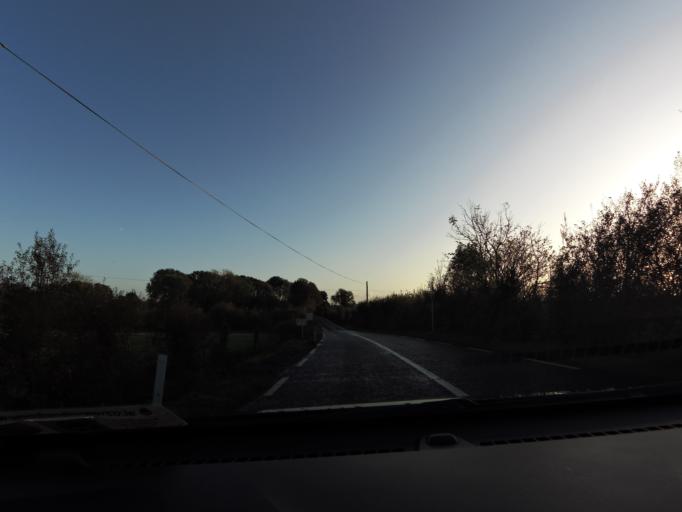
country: IE
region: Connaught
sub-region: Roscommon
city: Castlerea
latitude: 53.7170
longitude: -8.5625
